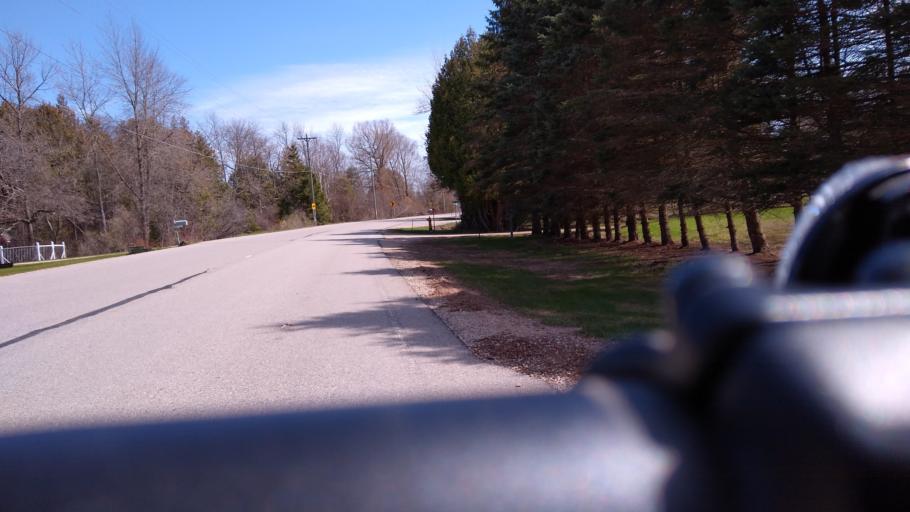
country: US
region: Michigan
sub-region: Delta County
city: Escanaba
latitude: 45.6817
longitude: -87.1449
